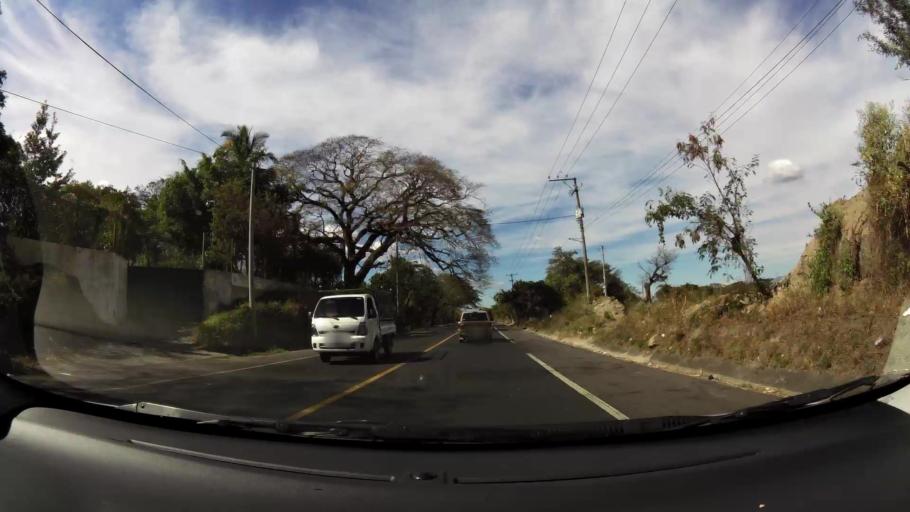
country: SV
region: San Salvador
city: Guazapa
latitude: 13.8629
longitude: -89.1659
